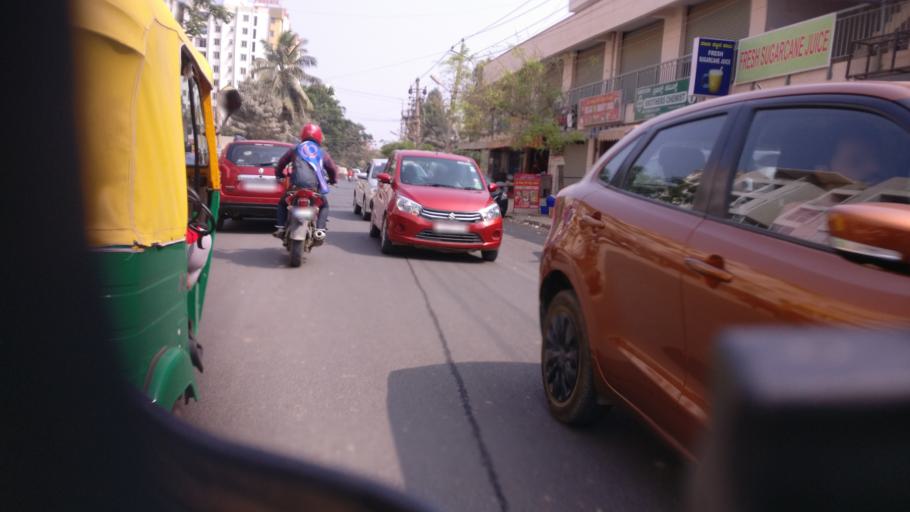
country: IN
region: Karnataka
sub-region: Bangalore Urban
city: Bangalore
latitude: 12.8996
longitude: 77.6755
